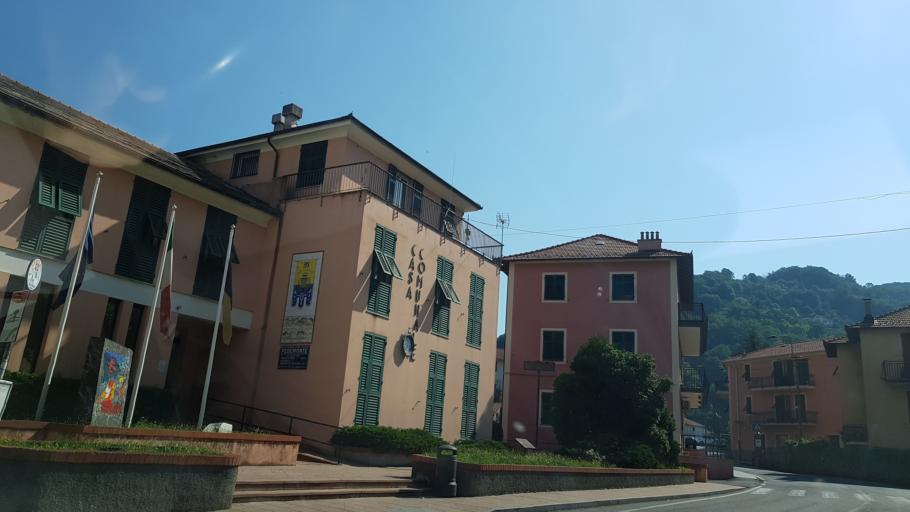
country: IT
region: Liguria
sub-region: Provincia di Genova
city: Serra Ricco
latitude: 44.5077
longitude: 8.9358
